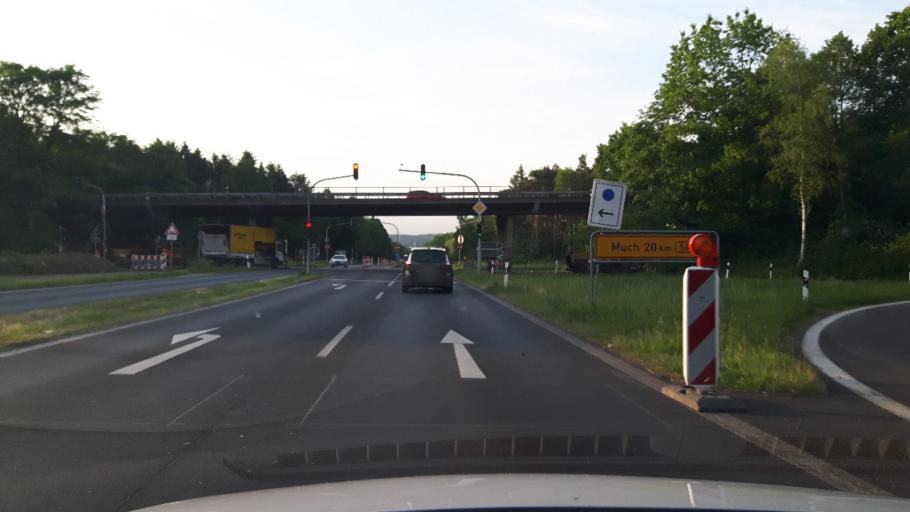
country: DE
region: North Rhine-Westphalia
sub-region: Regierungsbezirk Koln
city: Siegburg
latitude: 50.8146
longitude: 7.2052
